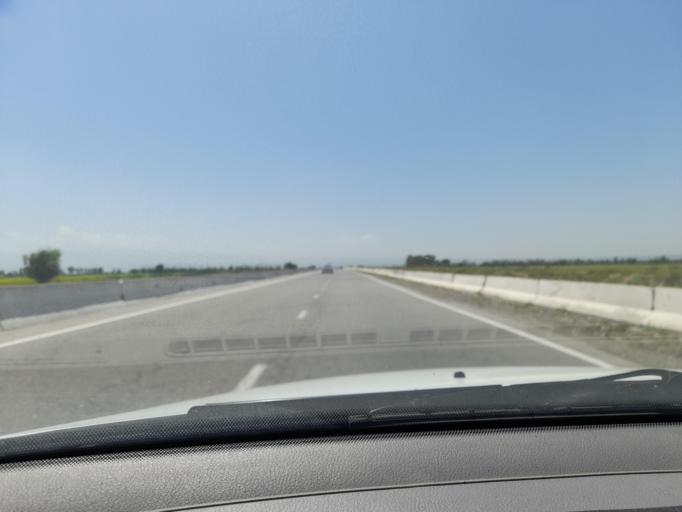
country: UZ
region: Jizzax
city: Paxtakor
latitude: 40.2184
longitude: 67.9899
